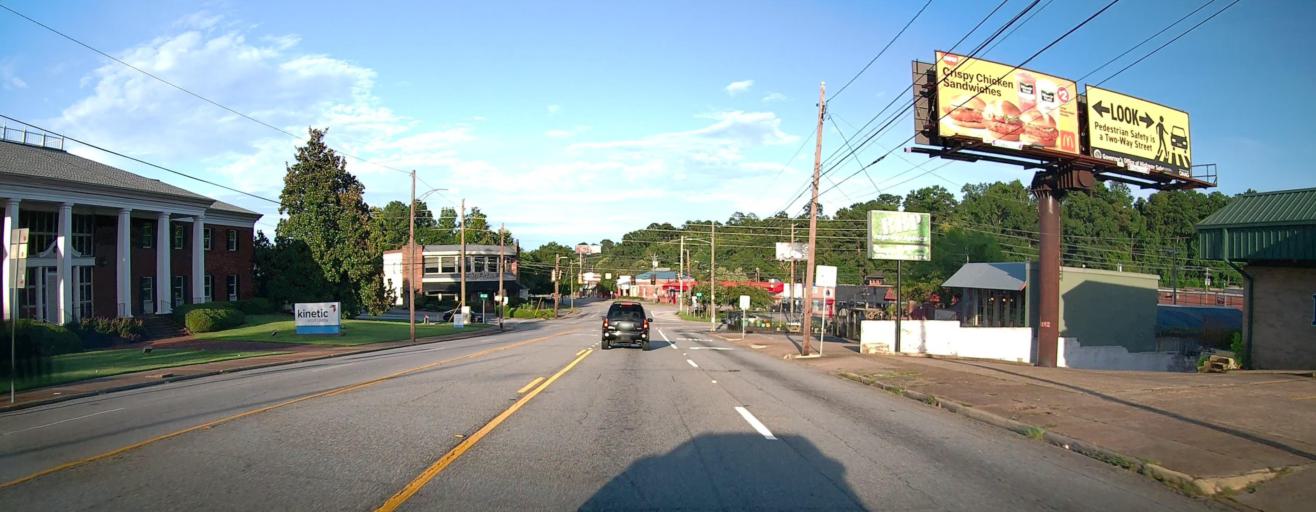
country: US
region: Georgia
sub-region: Muscogee County
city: Columbus
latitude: 32.4704
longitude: -84.9753
